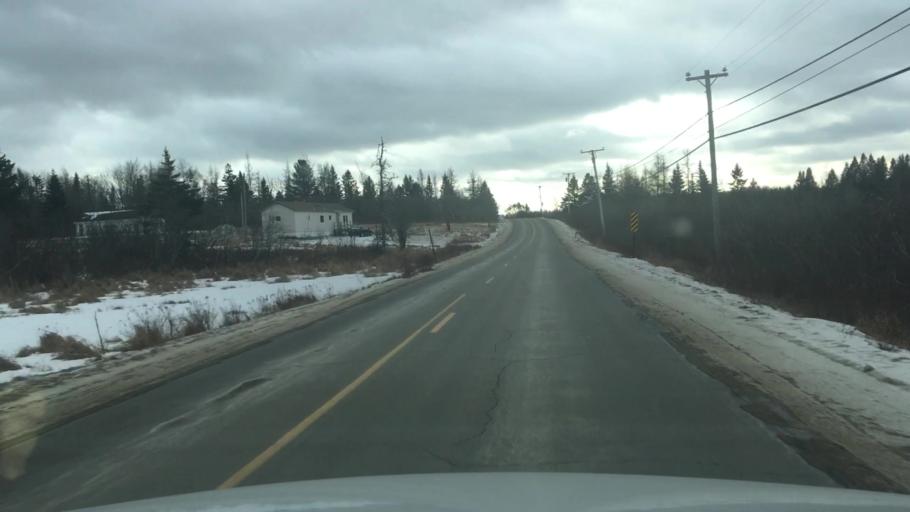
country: US
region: Maine
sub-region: Washington County
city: Machias
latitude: 44.6827
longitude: -67.4672
